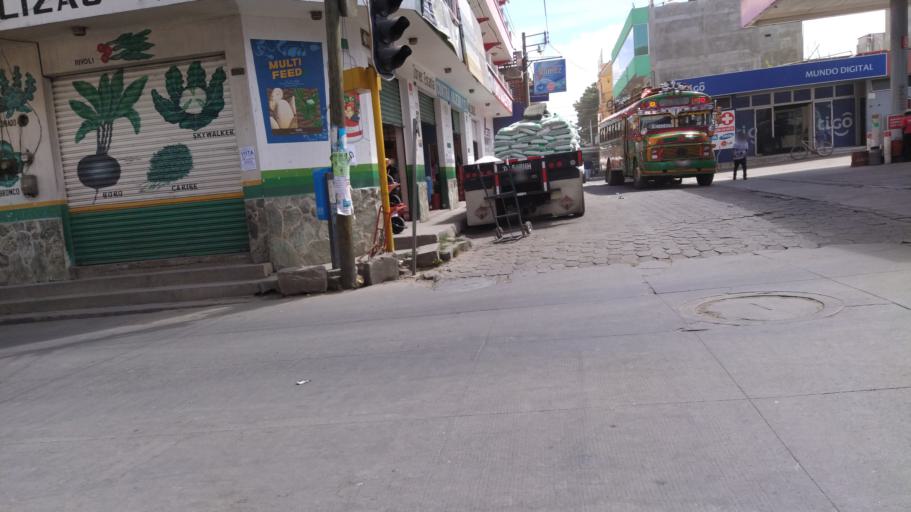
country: GT
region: Quetzaltenango
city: Ostuncalco
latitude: 14.8701
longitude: -91.6220
